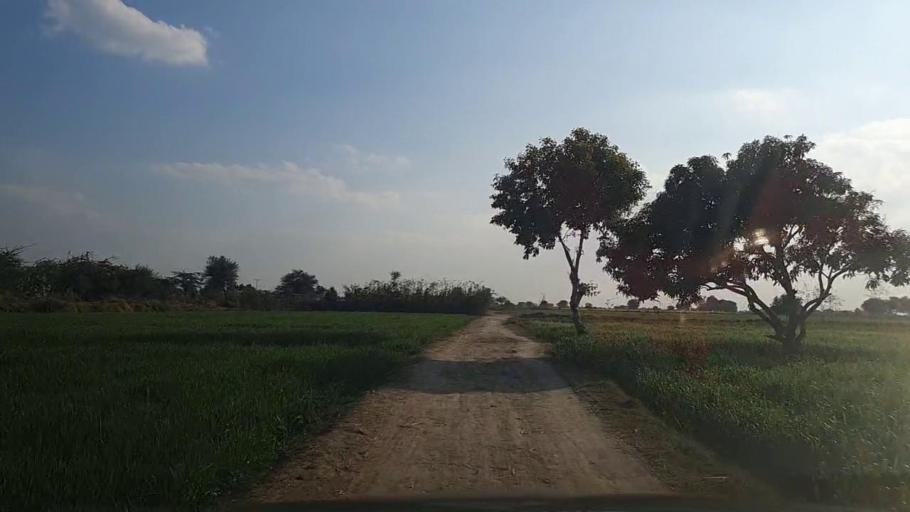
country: PK
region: Sindh
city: Jhol
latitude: 25.8346
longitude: 69.0516
